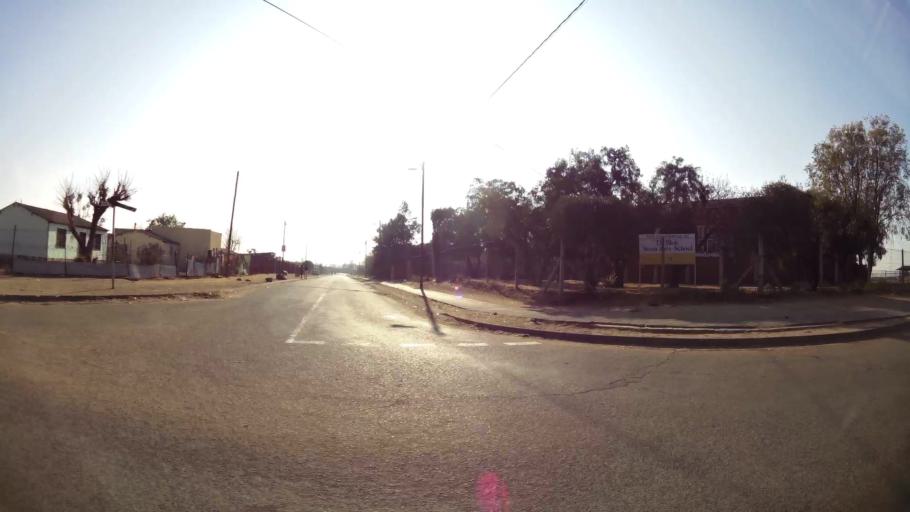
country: ZA
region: Orange Free State
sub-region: Mangaung Metropolitan Municipality
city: Bloemfontein
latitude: -29.1368
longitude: 26.2446
